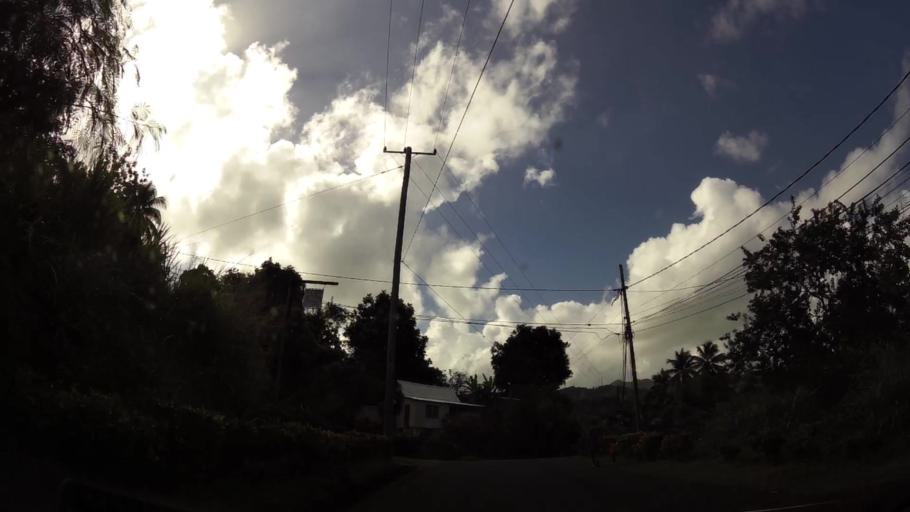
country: DM
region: Saint Andrew
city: Marigot
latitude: 15.5400
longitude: -61.2834
